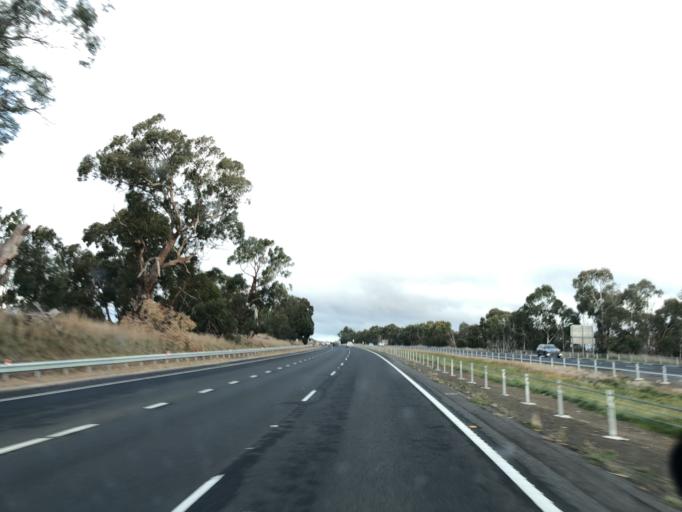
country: AU
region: Victoria
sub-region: Mount Alexander
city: Castlemaine
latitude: -37.2617
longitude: 144.4723
